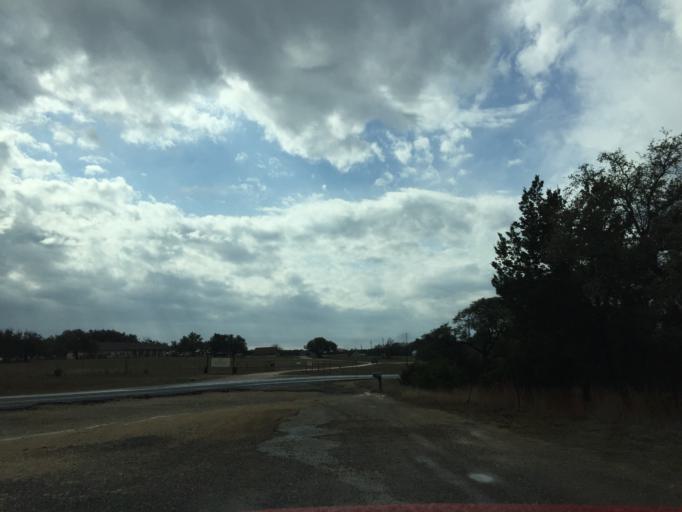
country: US
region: Texas
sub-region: Williamson County
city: Leander
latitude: 30.6322
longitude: -97.9729
